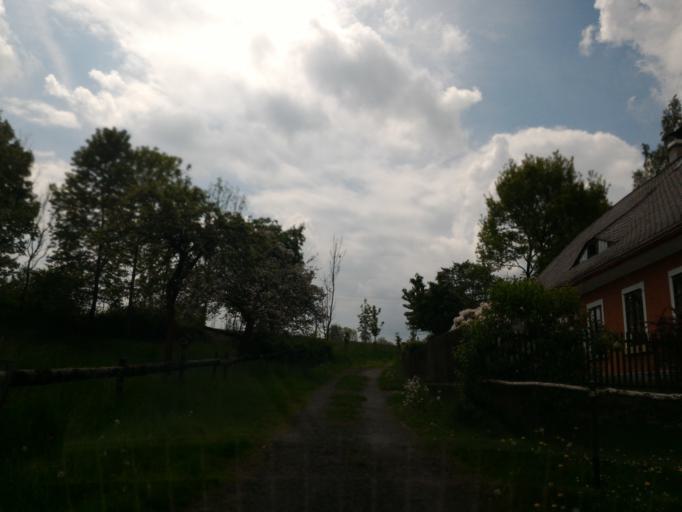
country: CZ
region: Ustecky
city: Varnsdorf
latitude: 50.9020
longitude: 14.6060
